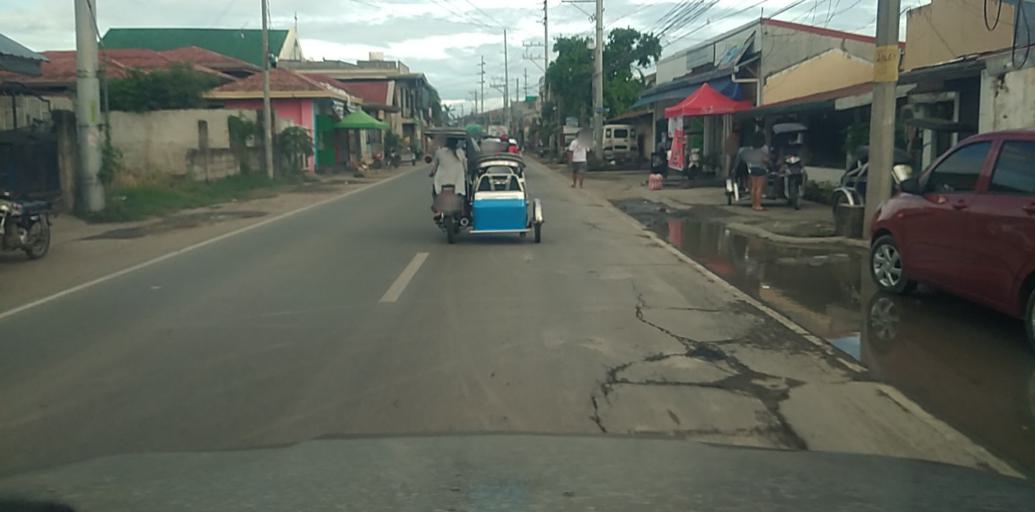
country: PH
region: Central Luzon
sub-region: Province of Pampanga
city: Arayat
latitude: 15.1467
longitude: 120.7653
